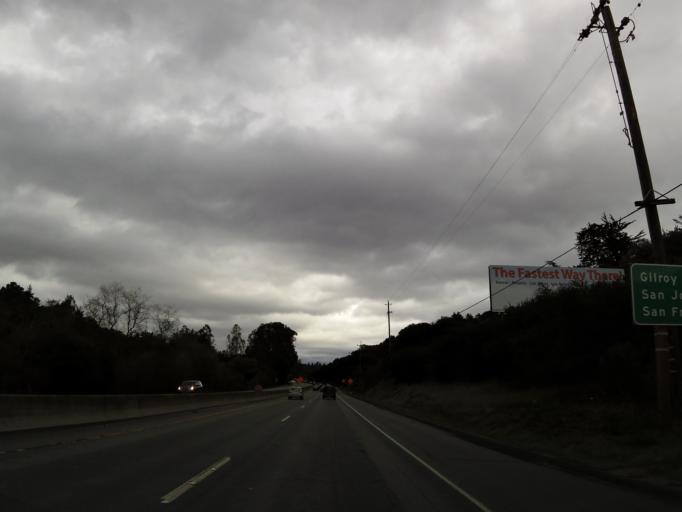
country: US
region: California
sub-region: Monterey County
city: Prunedale
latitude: 36.8071
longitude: -121.6479
